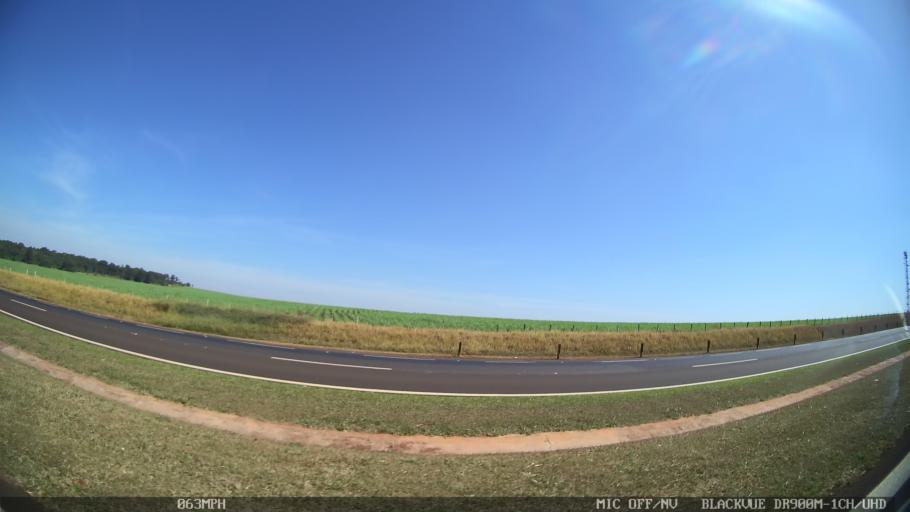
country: BR
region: Sao Paulo
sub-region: Ribeirao Preto
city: Ribeirao Preto
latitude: -21.1710
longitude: -47.8983
